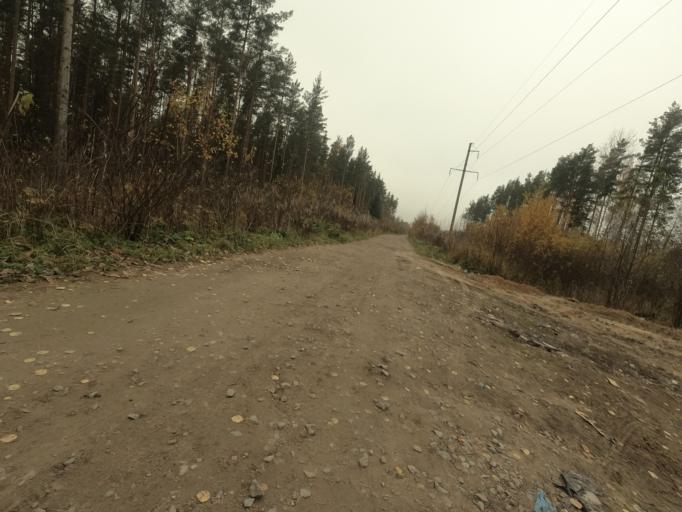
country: RU
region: Leningrad
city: Pavlovo
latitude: 59.7680
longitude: 30.9348
